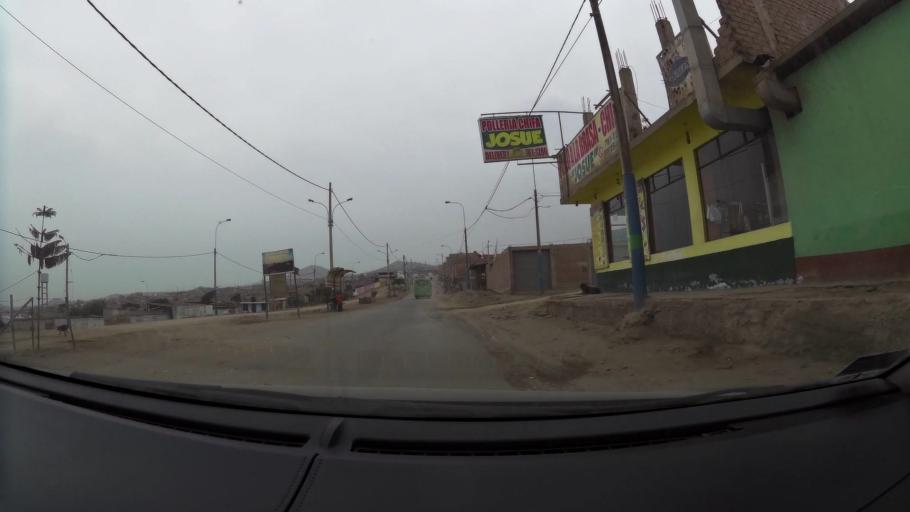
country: PE
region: Lima
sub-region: Lima
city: Santa Rosa
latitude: -11.8416
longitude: -77.1543
